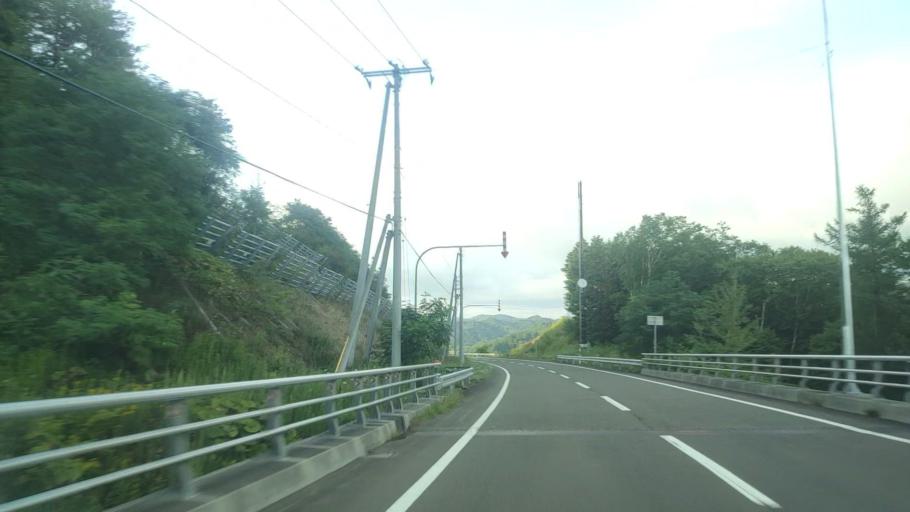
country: JP
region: Hokkaido
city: Bibai
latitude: 43.0680
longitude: 142.1036
